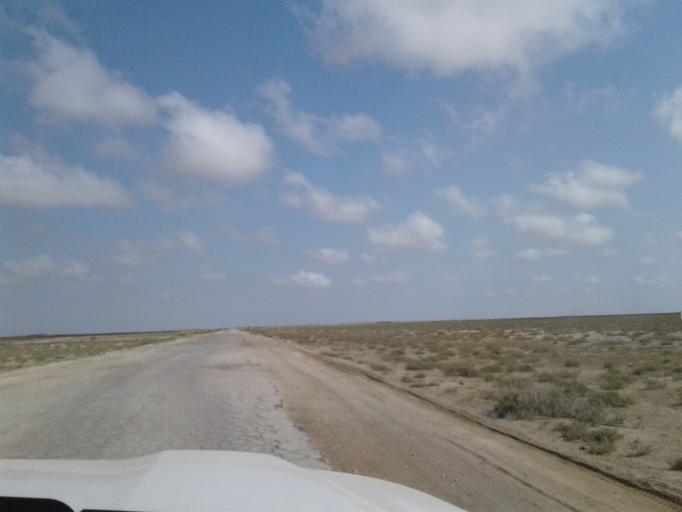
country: IR
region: Golestan
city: Gomishan
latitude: 37.6196
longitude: 53.9271
